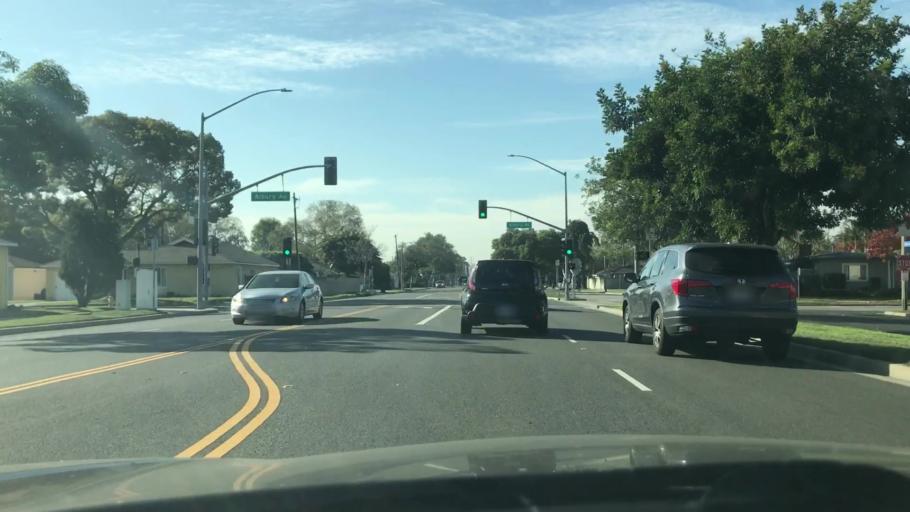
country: US
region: California
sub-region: Orange County
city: Rossmoor
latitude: 33.7960
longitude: -118.1174
